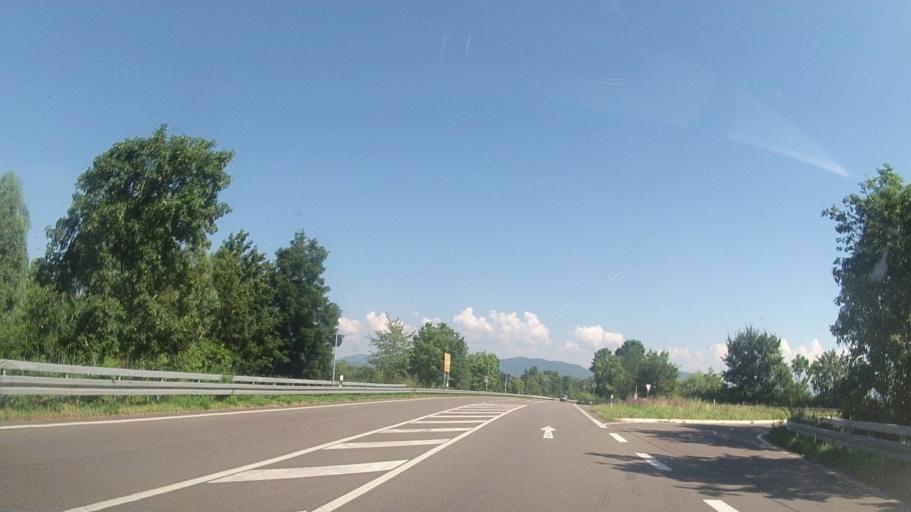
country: DE
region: Baden-Wuerttemberg
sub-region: Freiburg Region
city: Willstatt
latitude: 48.5342
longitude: 7.9221
